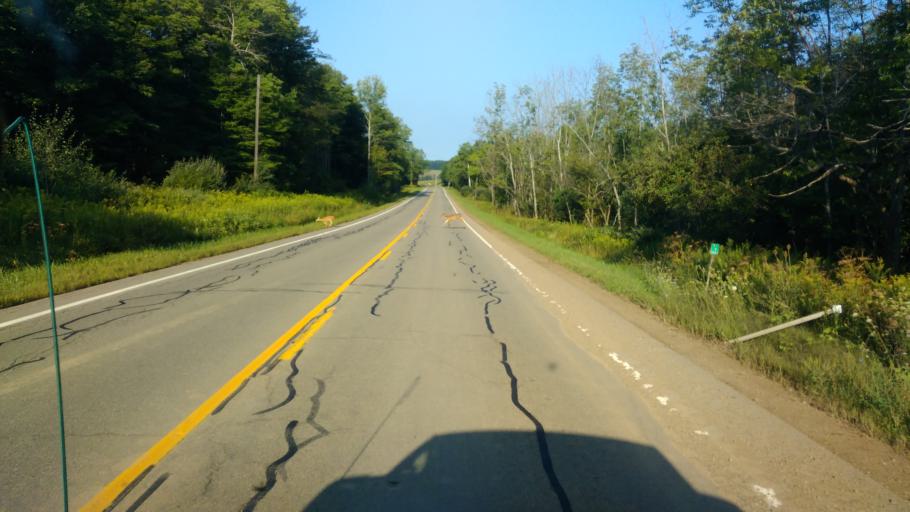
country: US
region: New York
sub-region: Allegany County
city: Andover
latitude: 42.1539
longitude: -77.7069
